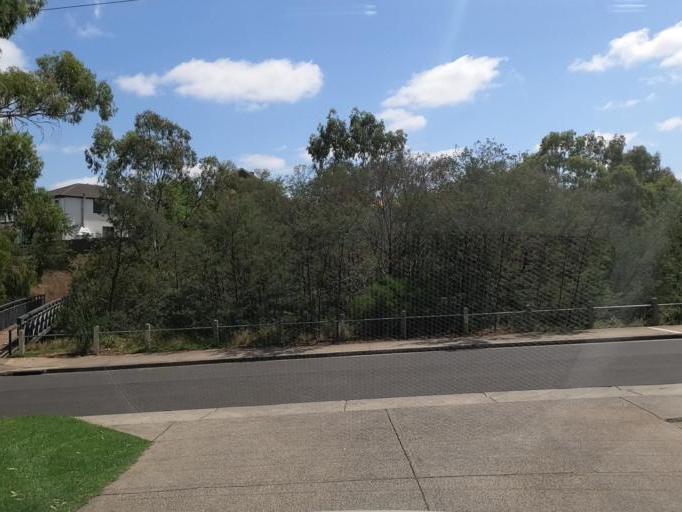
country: AU
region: Victoria
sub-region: Hume
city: Westmeadows
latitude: -37.6749
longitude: 144.8927
